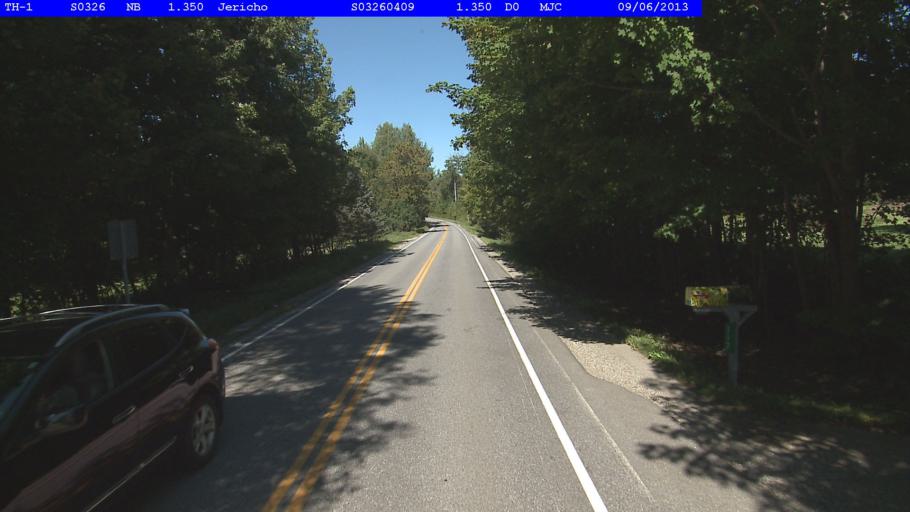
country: US
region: Vermont
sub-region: Chittenden County
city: Jericho
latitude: 44.4965
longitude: -72.9554
